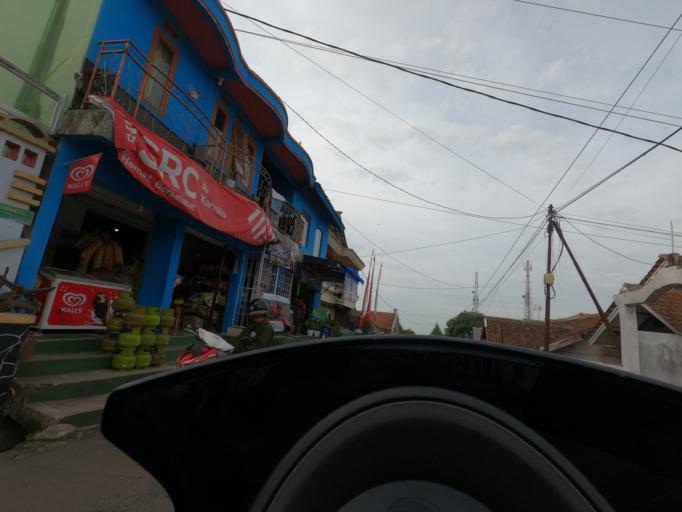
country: ID
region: West Java
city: Lembang
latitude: -6.7333
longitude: 107.6467
